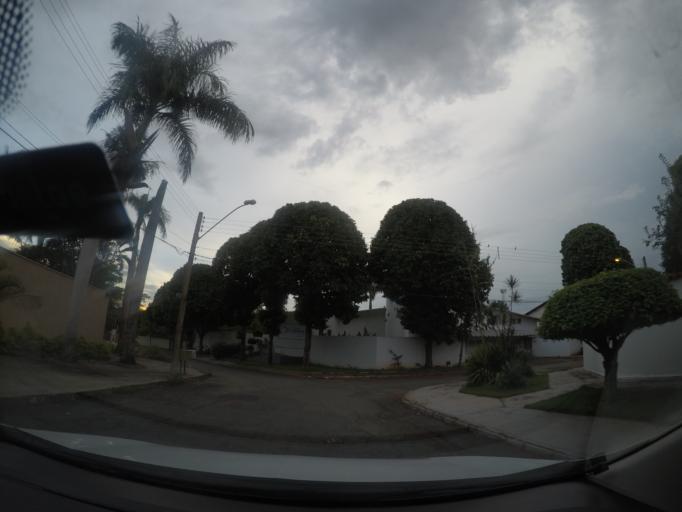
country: BR
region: Goias
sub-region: Goiania
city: Goiania
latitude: -16.6545
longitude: -49.2280
